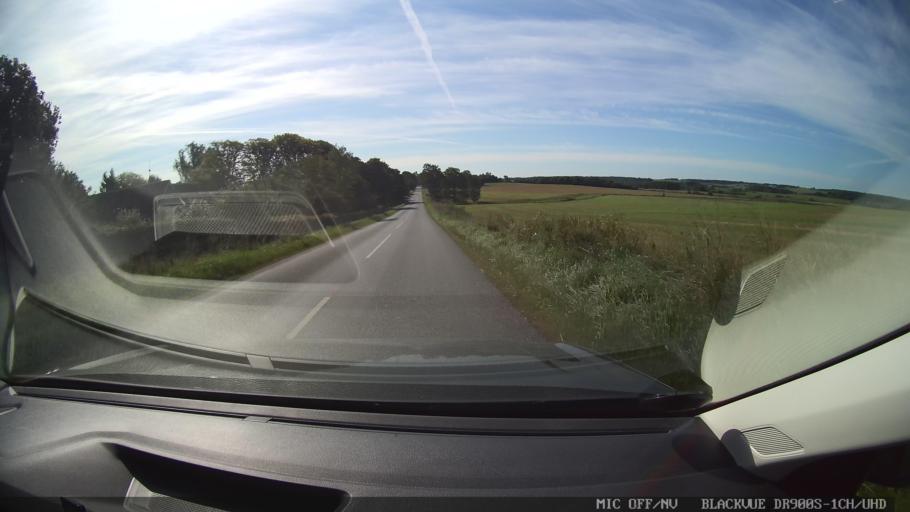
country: DK
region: North Denmark
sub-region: Mariagerfjord Kommune
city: Hobro
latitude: 56.5558
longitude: 9.8433
